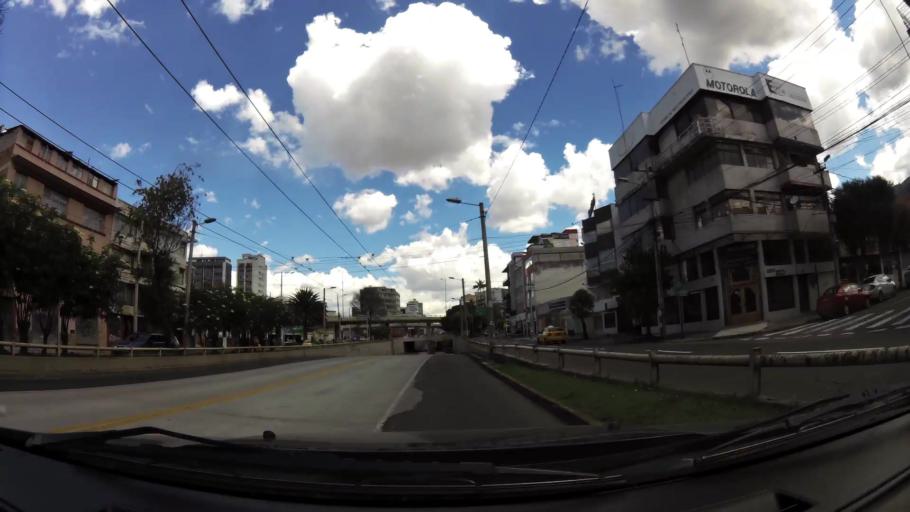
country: EC
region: Pichincha
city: Quito
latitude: -0.1945
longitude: -78.4945
